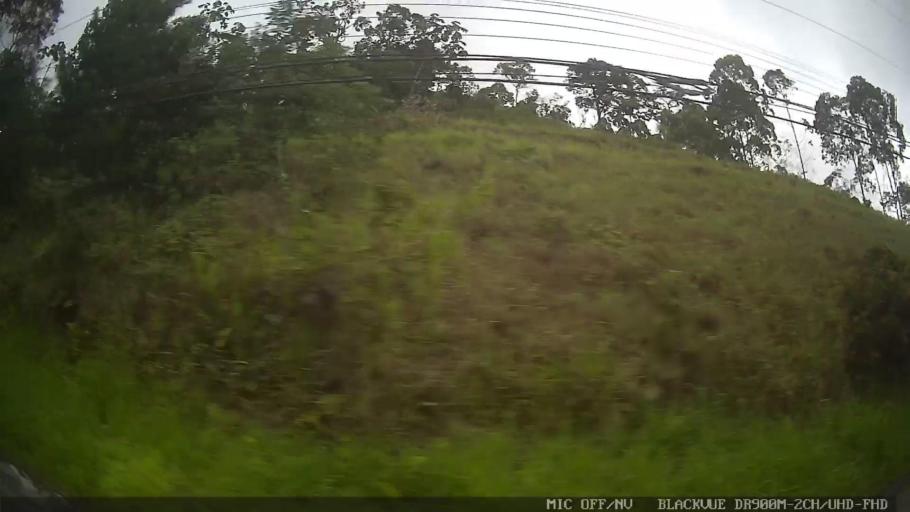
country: BR
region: Sao Paulo
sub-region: Mogi das Cruzes
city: Mogi das Cruzes
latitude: -23.4982
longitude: -46.2235
